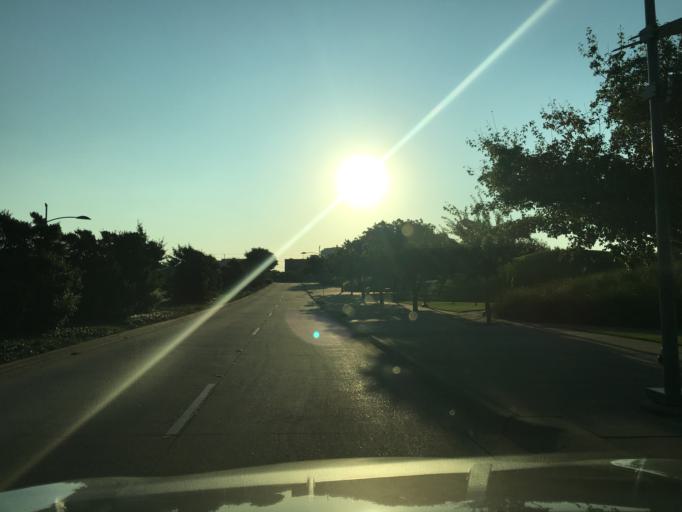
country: US
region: Texas
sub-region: Dallas County
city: Addison
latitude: 32.9570
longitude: -96.8326
